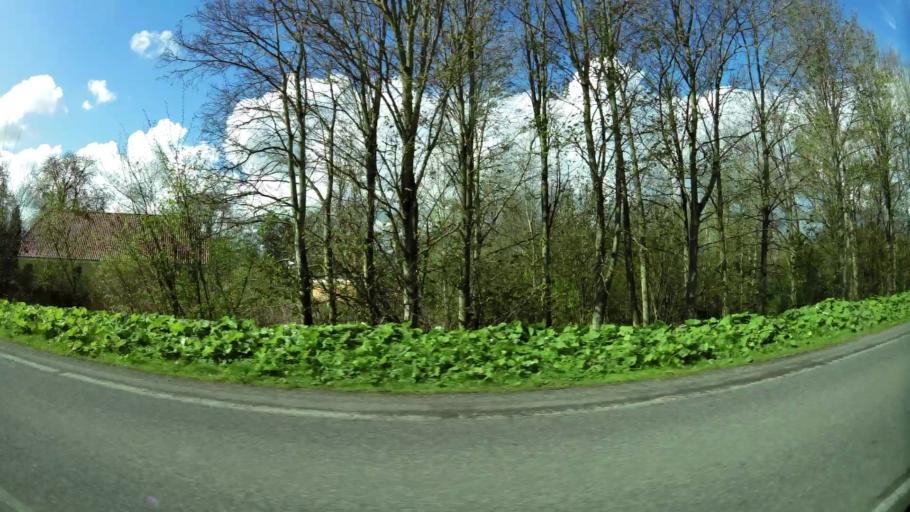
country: DK
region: South Denmark
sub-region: Middelfart Kommune
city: Brenderup
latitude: 55.4818
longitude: 9.9827
